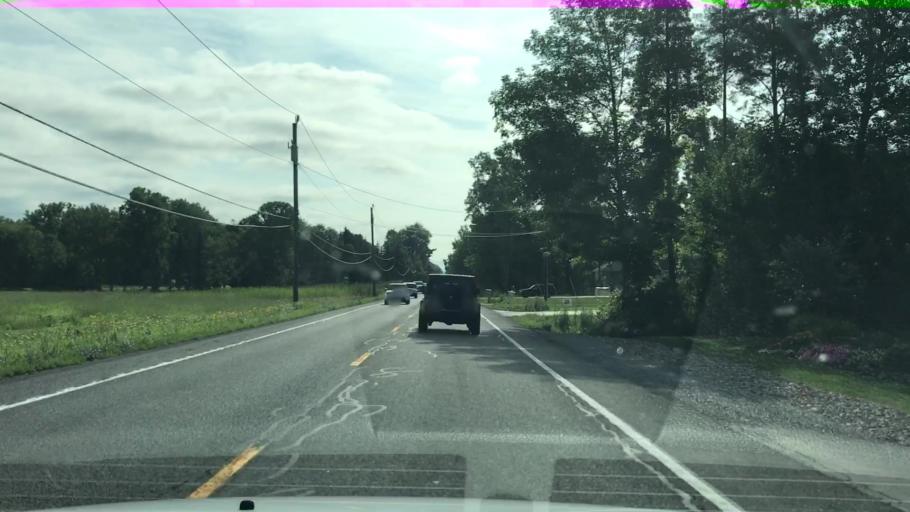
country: US
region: New York
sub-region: Erie County
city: Town Line
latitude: 42.8560
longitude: -78.5995
